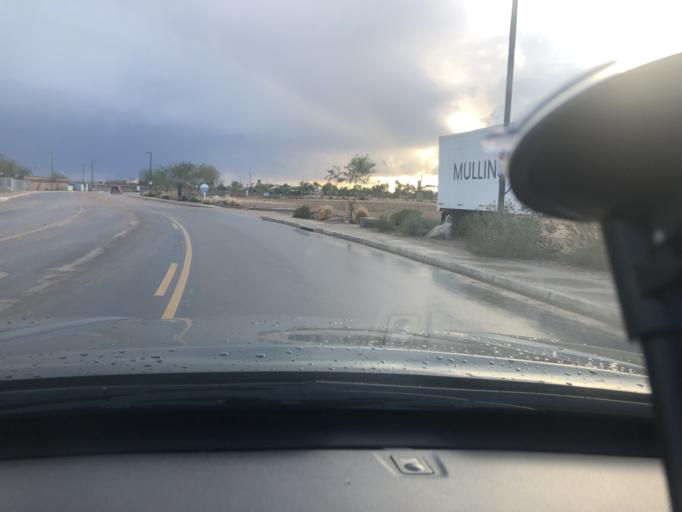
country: US
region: Arizona
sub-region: Maricopa County
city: Scottsdale
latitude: 33.4877
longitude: -111.8897
